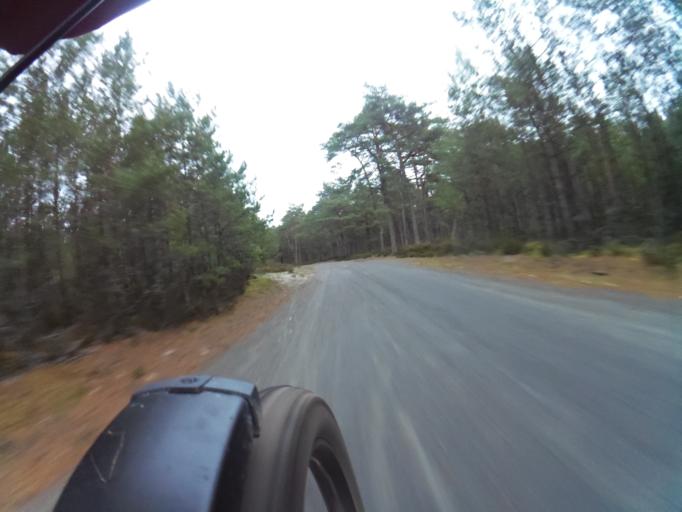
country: PL
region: Pomeranian Voivodeship
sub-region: Powiat wejherowski
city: Choczewo
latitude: 54.7913
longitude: 17.7595
